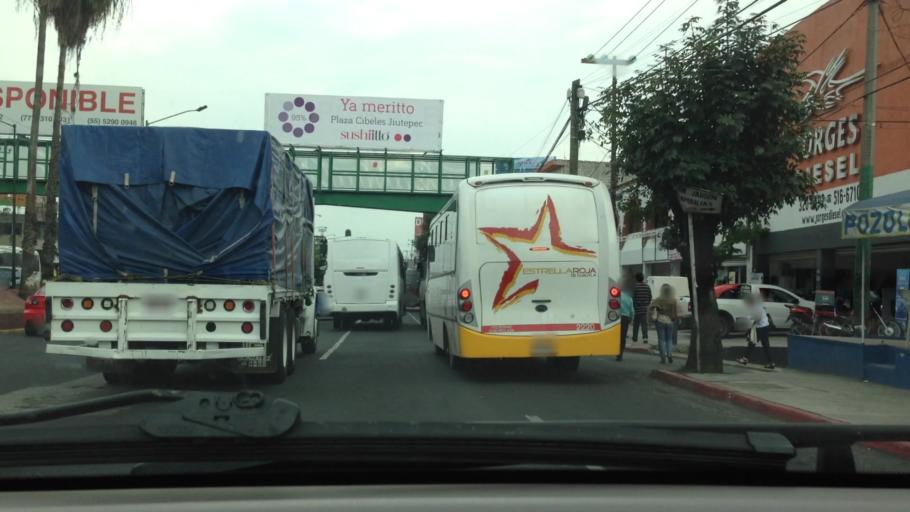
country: MX
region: Morelos
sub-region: Tepoztlan
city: Loma Bonita
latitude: 18.9170
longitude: -99.1871
